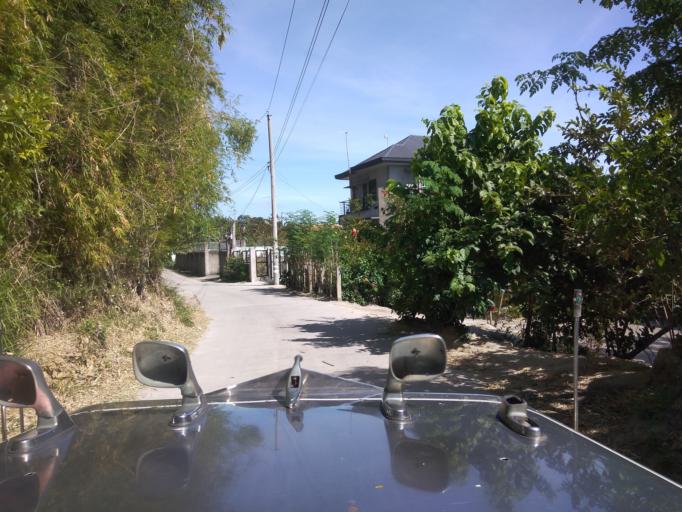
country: PH
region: Central Luzon
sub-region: Province of Pampanga
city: Magliman
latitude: 15.0263
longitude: 120.6538
